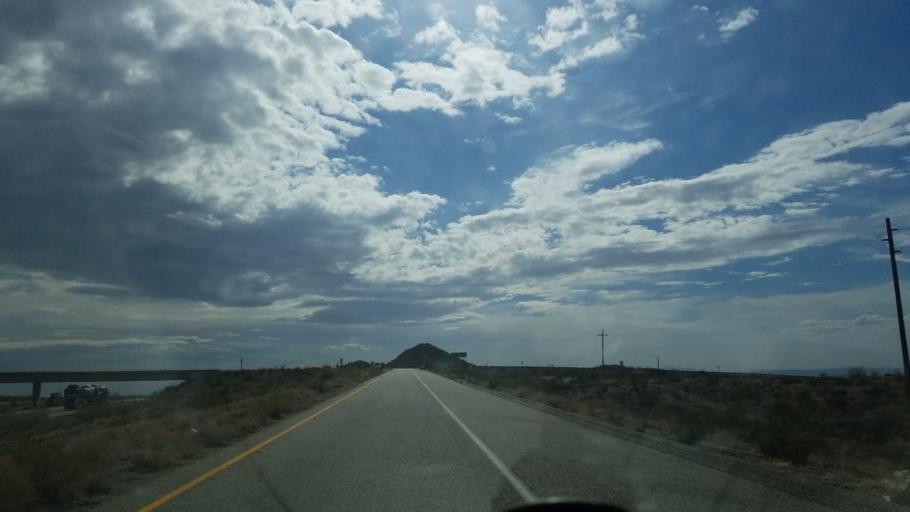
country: US
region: California
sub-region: San Bernardino County
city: Needles
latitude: 34.8311
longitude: -115.0490
